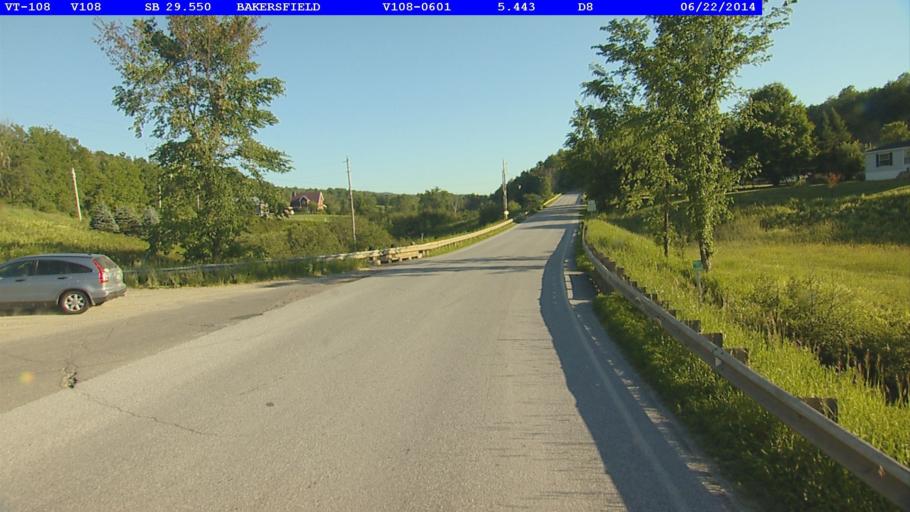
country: US
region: Vermont
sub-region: Franklin County
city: Enosburg Falls
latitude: 44.8052
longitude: -72.7876
